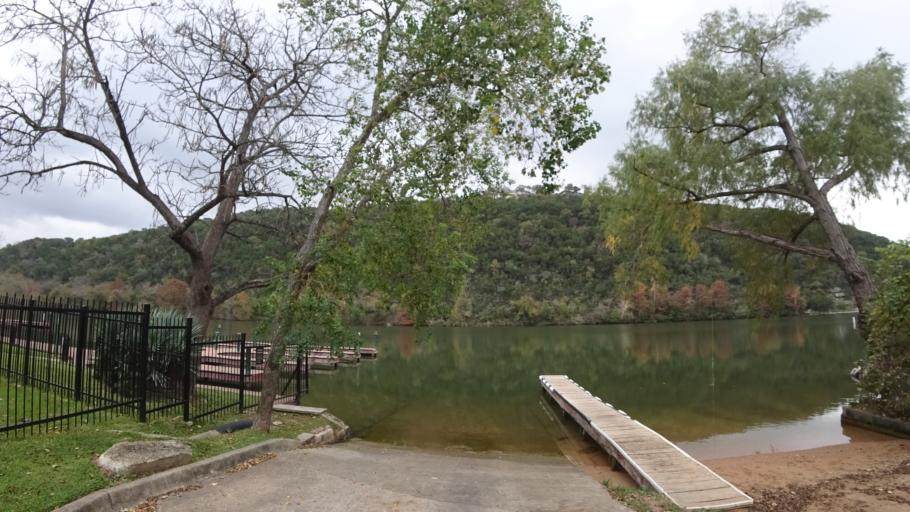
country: US
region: Texas
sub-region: Travis County
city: Bee Cave
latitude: 30.3273
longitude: -97.9178
